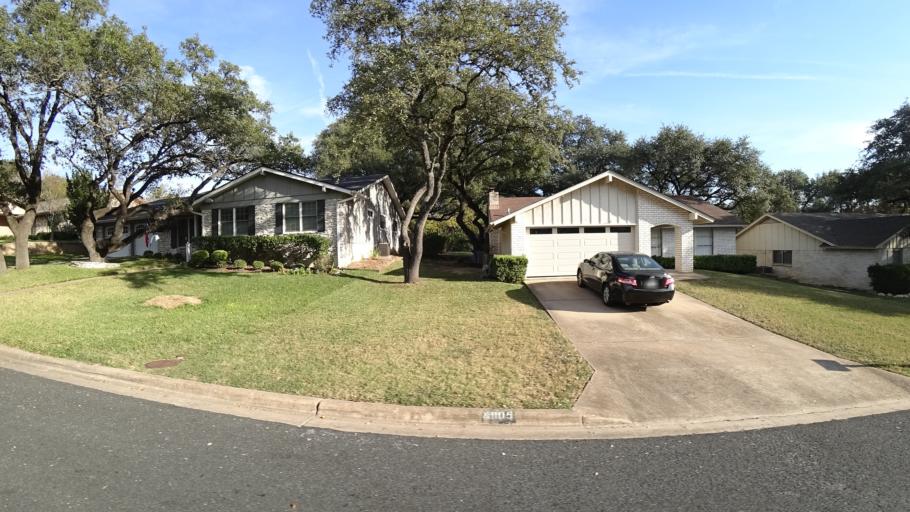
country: US
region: Texas
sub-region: Williamson County
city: Jollyville
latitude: 30.3689
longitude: -97.7532
